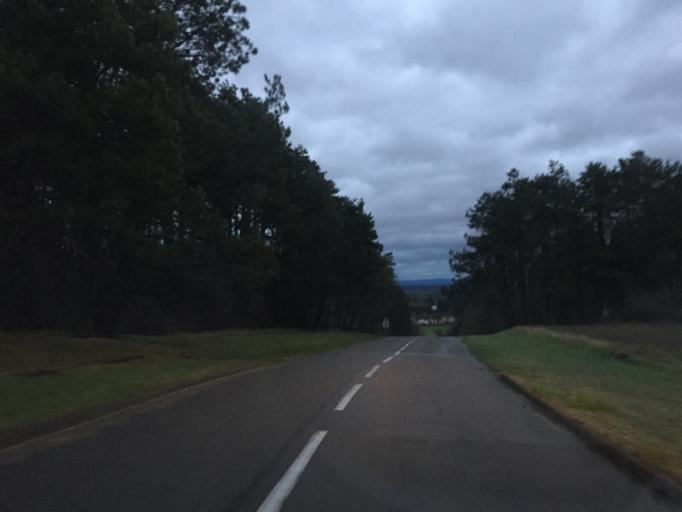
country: FR
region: Franche-Comte
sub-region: Departement du Jura
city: Champvans
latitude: 47.1115
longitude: 5.4688
